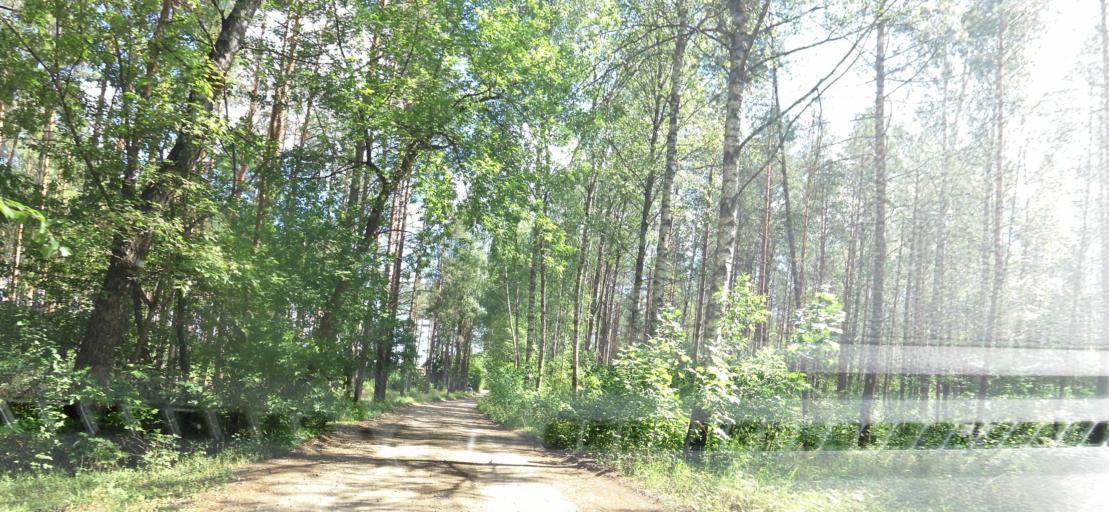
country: LT
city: Nemencine
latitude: 54.8181
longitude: 25.3905
